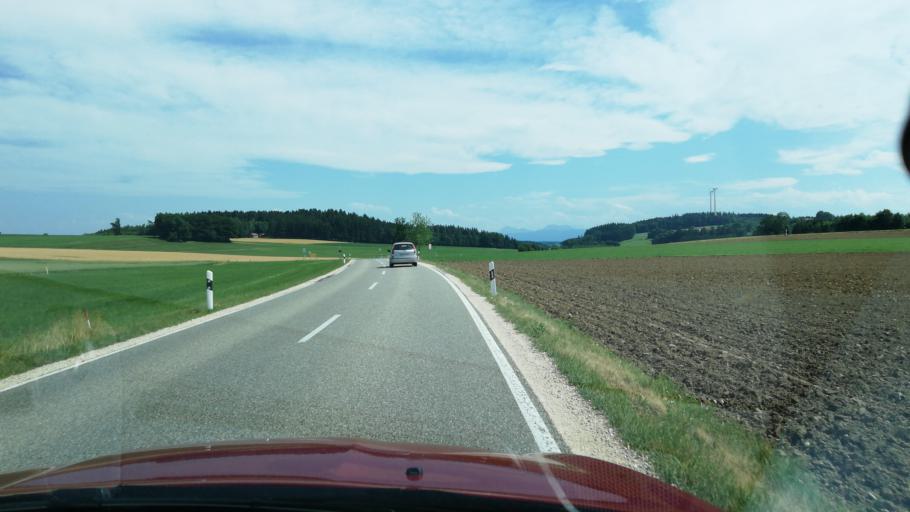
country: DE
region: Bavaria
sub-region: Upper Bavaria
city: Palling
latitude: 48.0392
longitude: 12.6245
